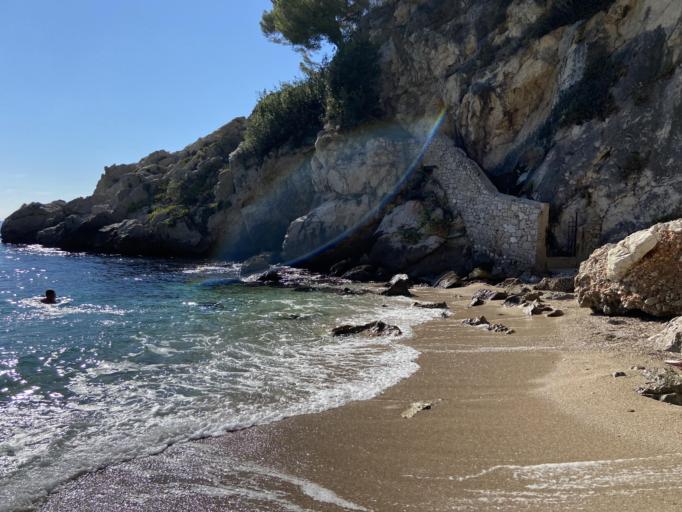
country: FR
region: Provence-Alpes-Cote d'Azur
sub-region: Departement des Alpes-Maritimes
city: Eze
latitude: 43.7221
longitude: 7.3809
